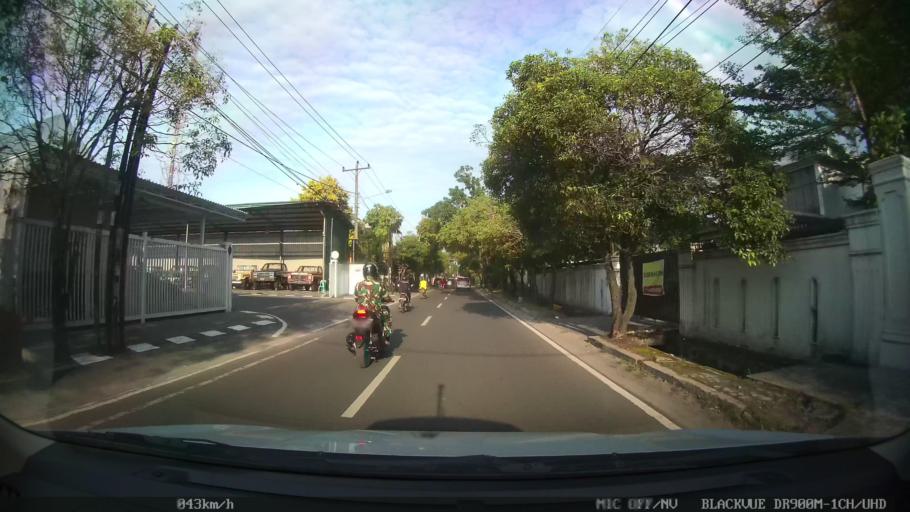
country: ID
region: North Sumatra
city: Medan
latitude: 3.5771
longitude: 98.6505
